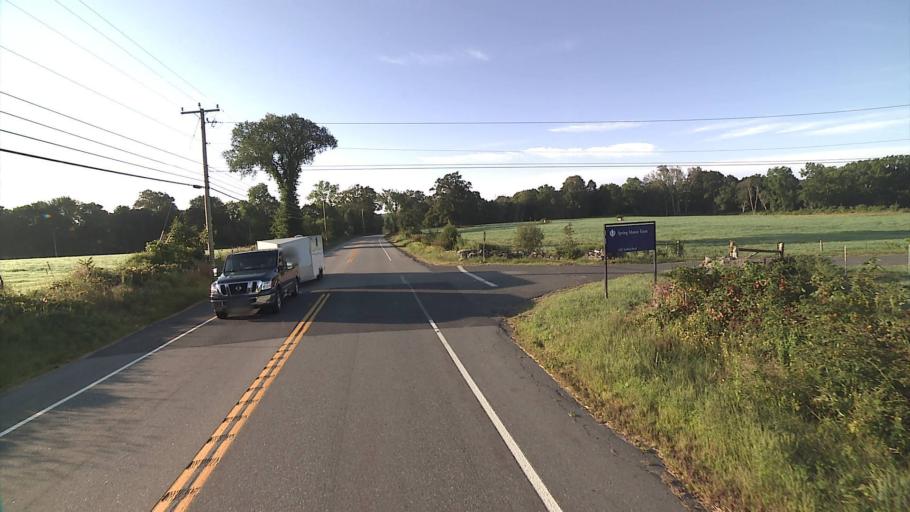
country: US
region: Connecticut
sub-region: Tolland County
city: South Coventry
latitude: 41.8086
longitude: -72.3056
